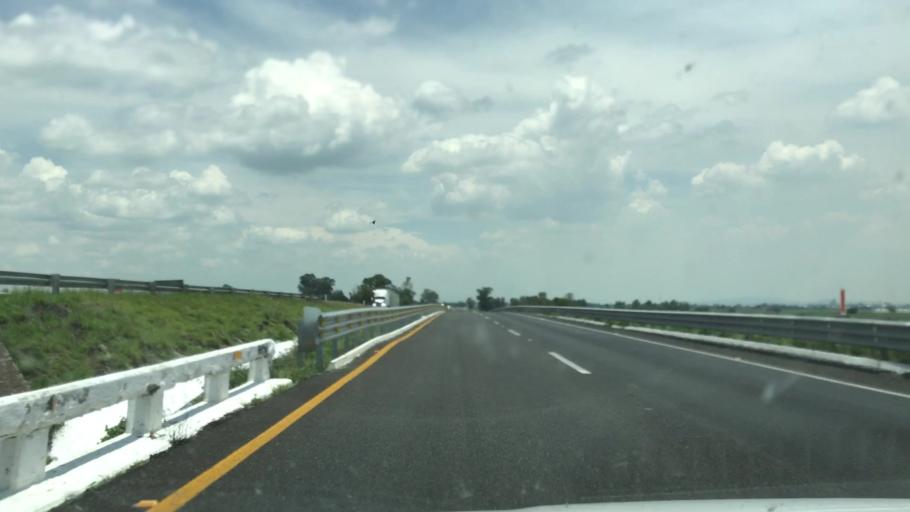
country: MX
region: Guanajuato
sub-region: Irapuato
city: Cuarta Brigada
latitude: 20.6452
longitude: -101.2736
